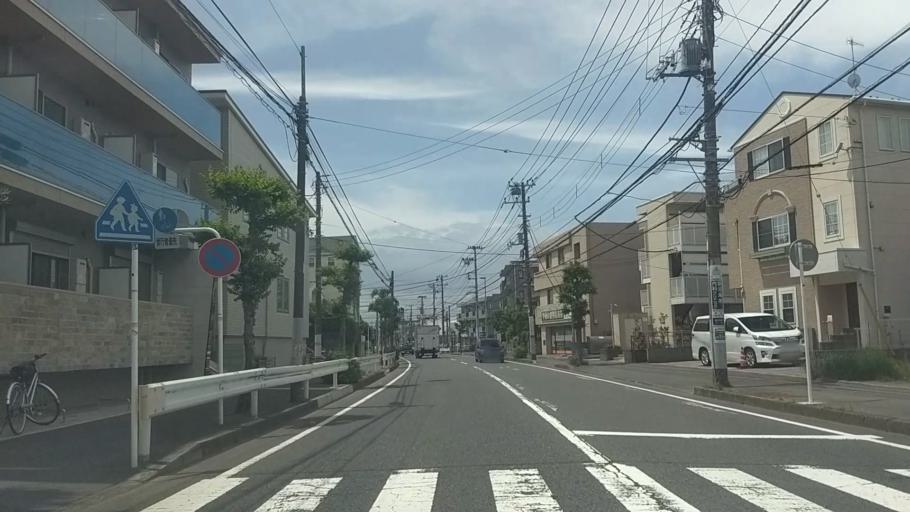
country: JP
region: Kanagawa
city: Fujisawa
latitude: 35.3257
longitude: 139.4669
